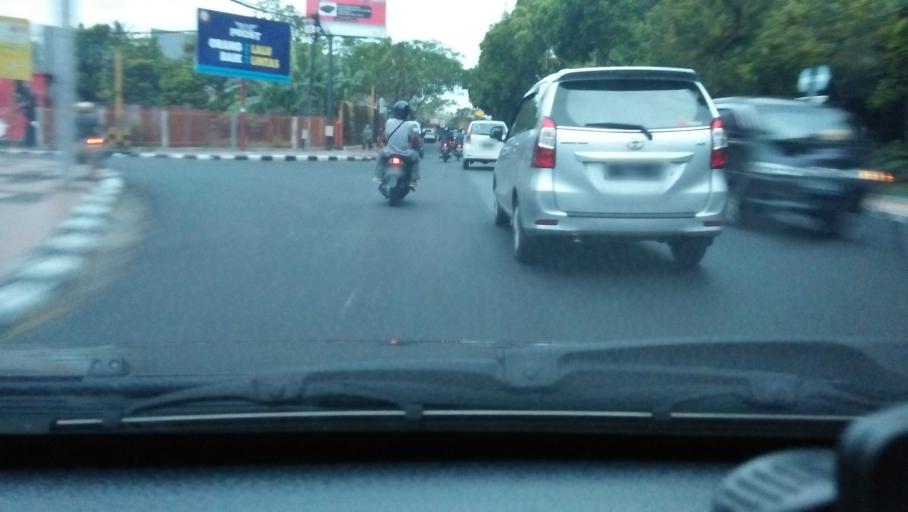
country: ID
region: Central Java
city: Magelang
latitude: -7.4940
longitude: 110.2230
